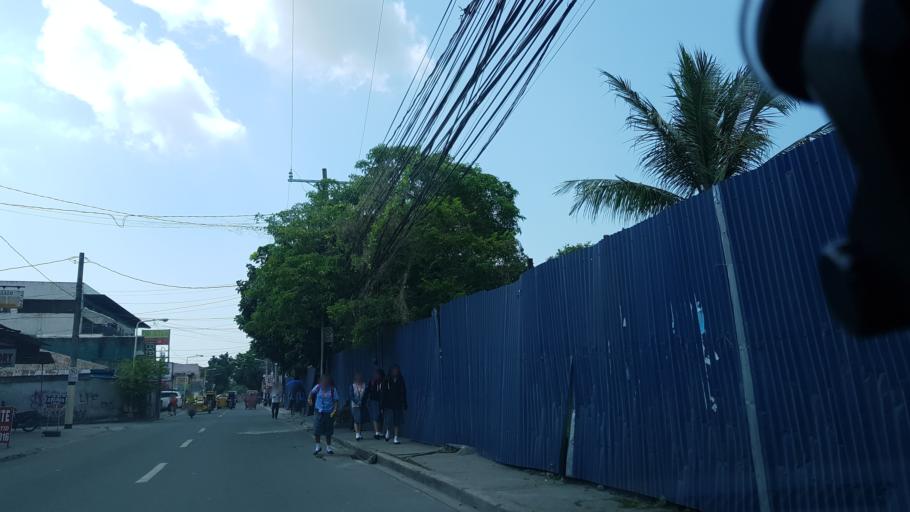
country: PH
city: Sambayanihan People's Village
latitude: 14.4633
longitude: 120.9887
